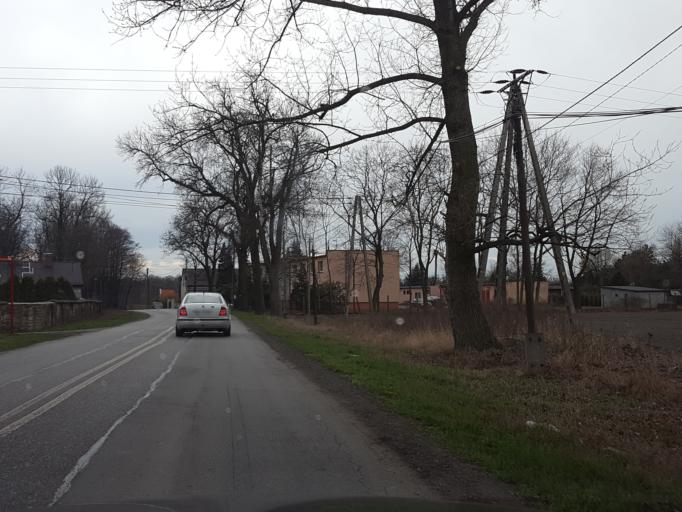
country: PL
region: Silesian Voivodeship
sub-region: Powiat gliwicki
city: Paniowki
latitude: 50.2090
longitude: 18.8137
